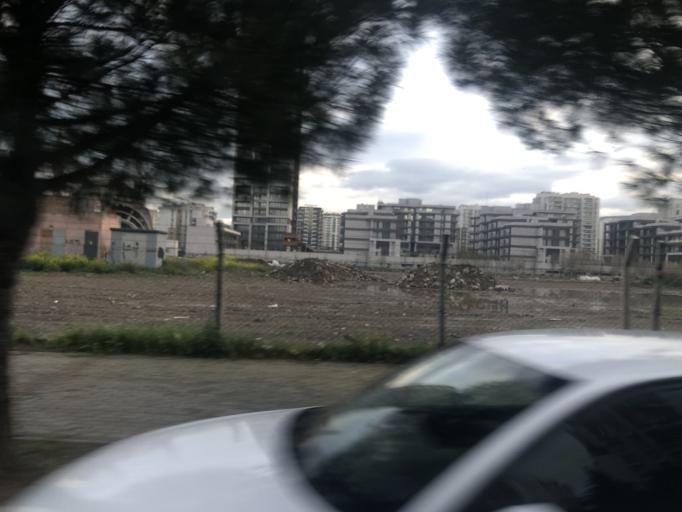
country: TR
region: Izmir
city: Karsiyaka
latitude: 38.4724
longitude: 27.0697
